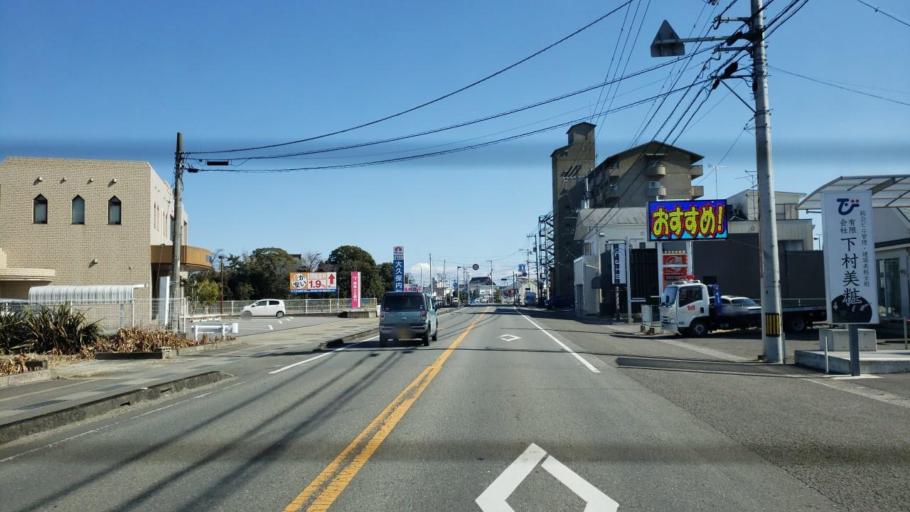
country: JP
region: Tokushima
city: Tokushima-shi
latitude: 34.1319
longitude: 134.5208
